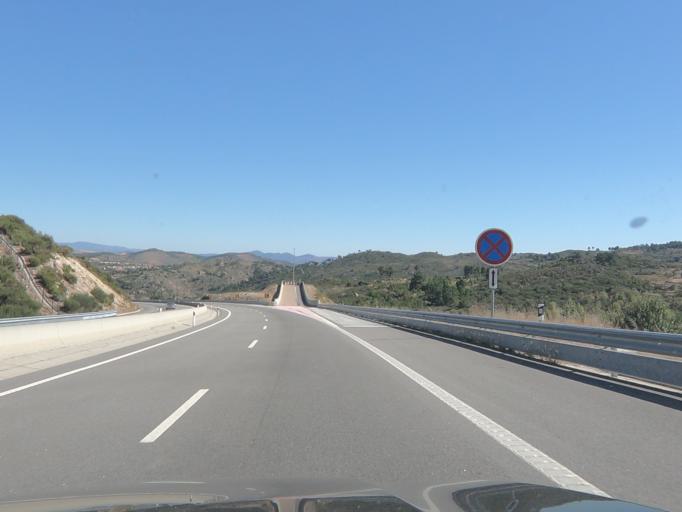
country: PT
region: Vila Real
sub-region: Murca
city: Murca
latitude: 41.3882
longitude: -7.4667
